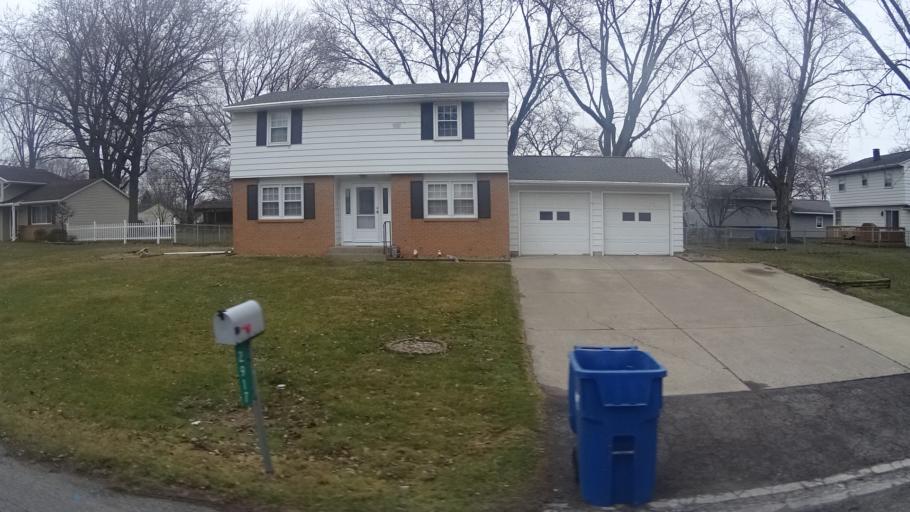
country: US
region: Ohio
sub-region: Erie County
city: Sandusky
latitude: 41.4224
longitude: -82.6529
